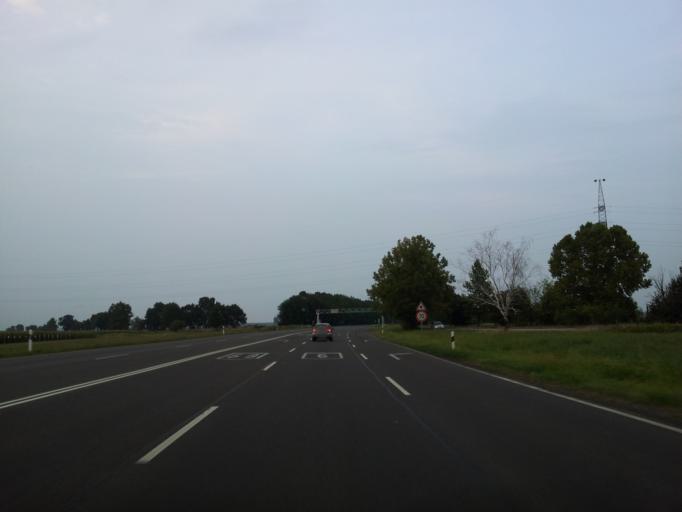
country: HU
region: Tolna
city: Szekszard
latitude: 46.4025
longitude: 18.7167
